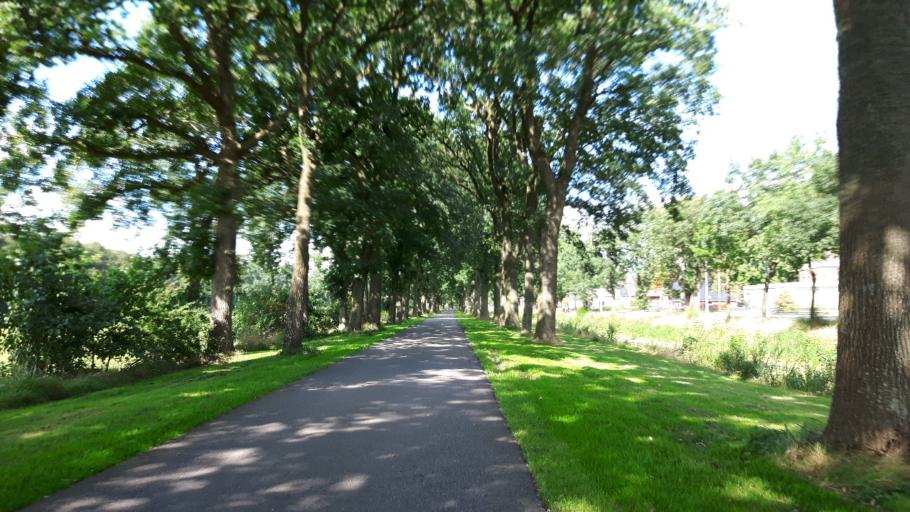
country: NL
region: Friesland
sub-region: Gemeente Smallingerland
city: Drachtstercompagnie
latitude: 53.0769
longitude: 6.2607
